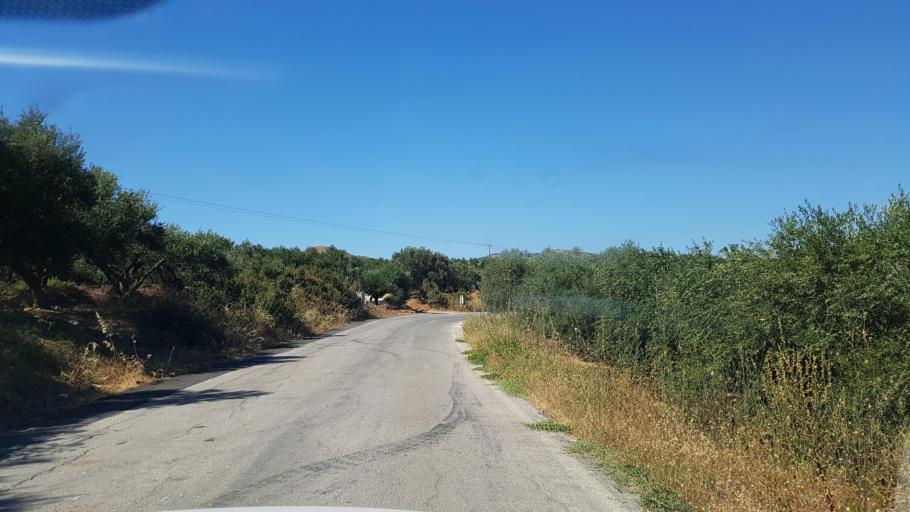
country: GR
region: Crete
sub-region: Nomos Chanias
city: Kissamos
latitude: 35.5003
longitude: 23.7231
